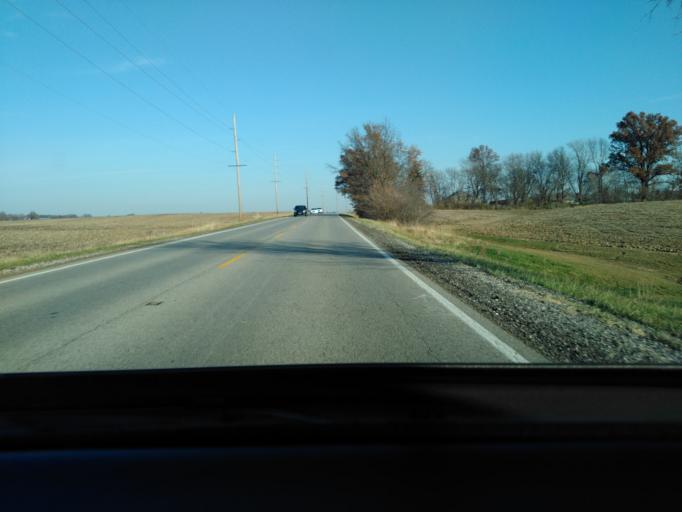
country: US
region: Illinois
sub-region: Madison County
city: Saint Jacob
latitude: 38.7343
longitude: -89.8013
